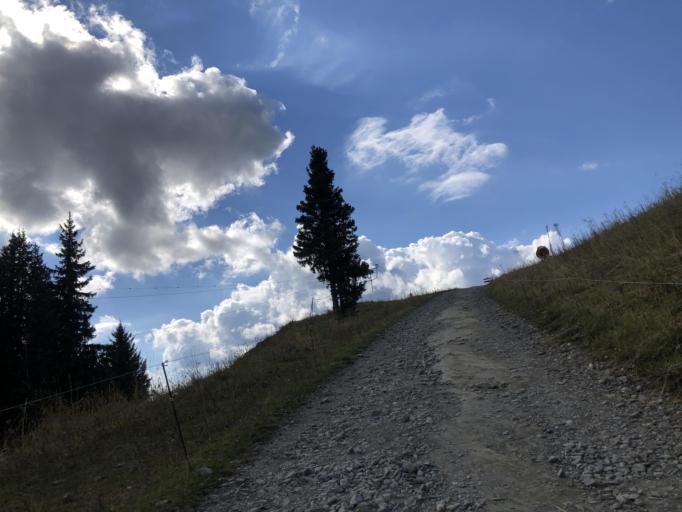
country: FR
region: Rhone-Alpes
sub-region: Departement de la Haute-Savoie
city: Les Contamines-Montjoie
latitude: 45.8458
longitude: 6.6769
